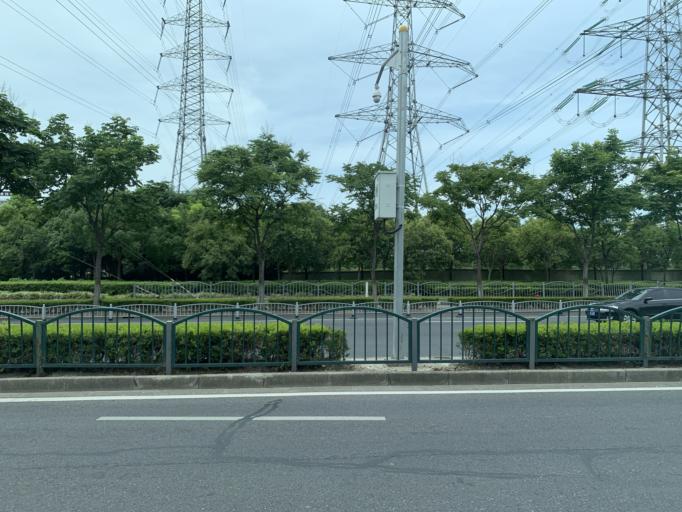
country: CN
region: Shanghai Shi
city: Kangqiao
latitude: 31.1635
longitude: 121.5594
